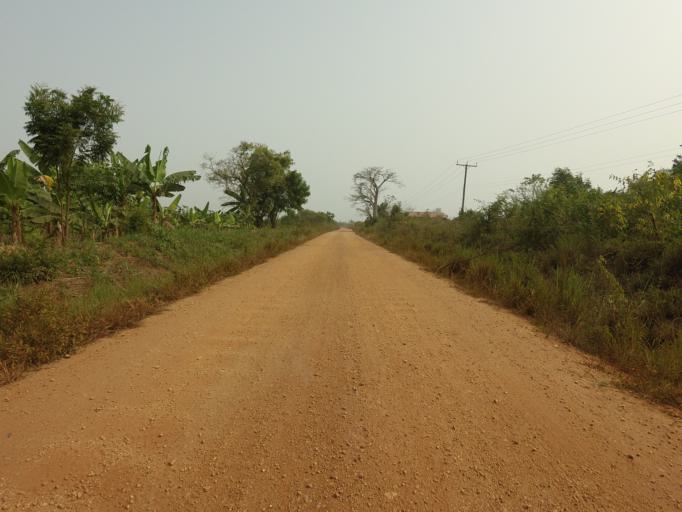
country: GH
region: Volta
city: Anloga
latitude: 5.9771
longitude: 0.6066
